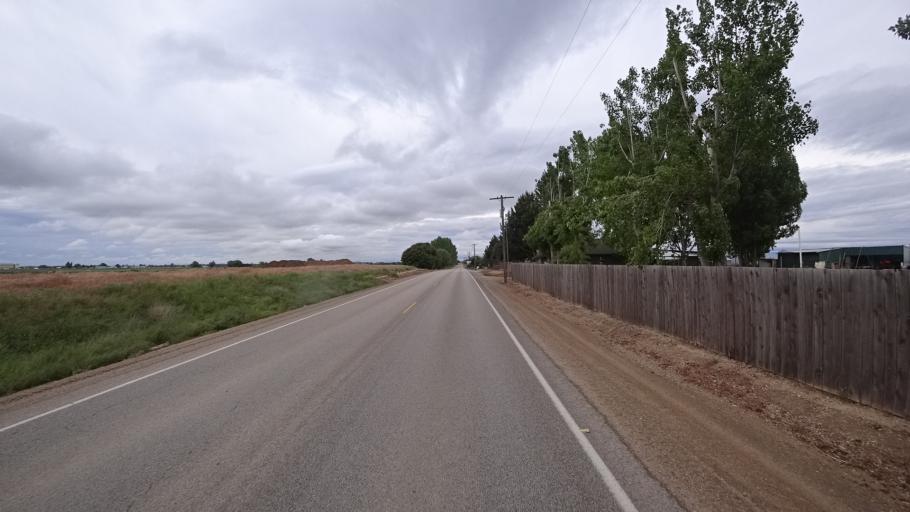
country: US
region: Idaho
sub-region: Ada County
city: Star
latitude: 43.6425
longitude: -116.4935
